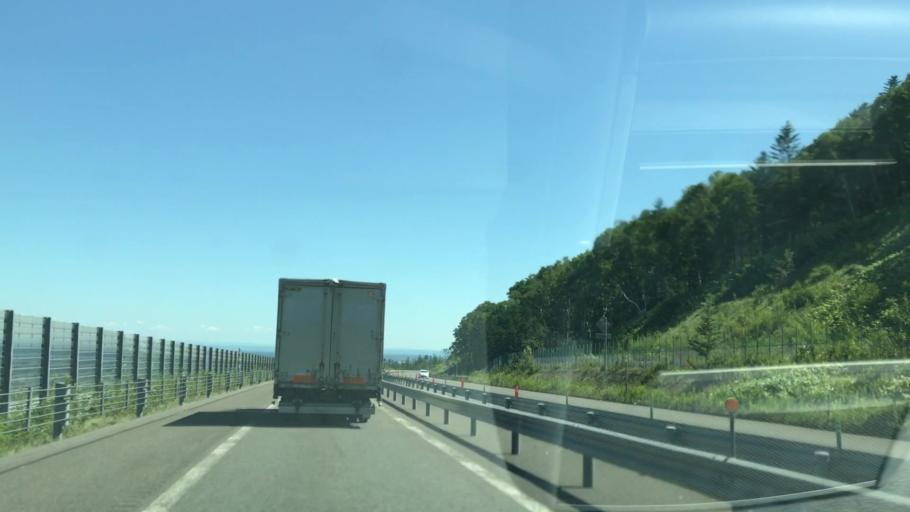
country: JP
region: Hokkaido
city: Otofuke
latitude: 43.0708
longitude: 142.7541
